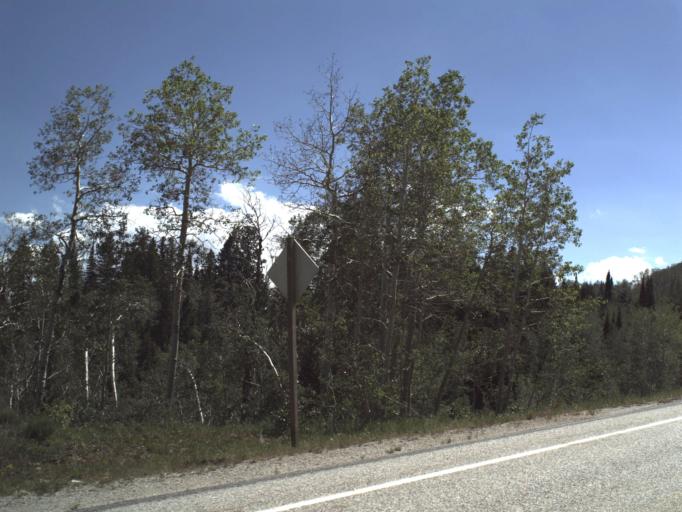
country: US
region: Utah
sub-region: Rich County
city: Randolph
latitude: 41.4765
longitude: -111.4673
